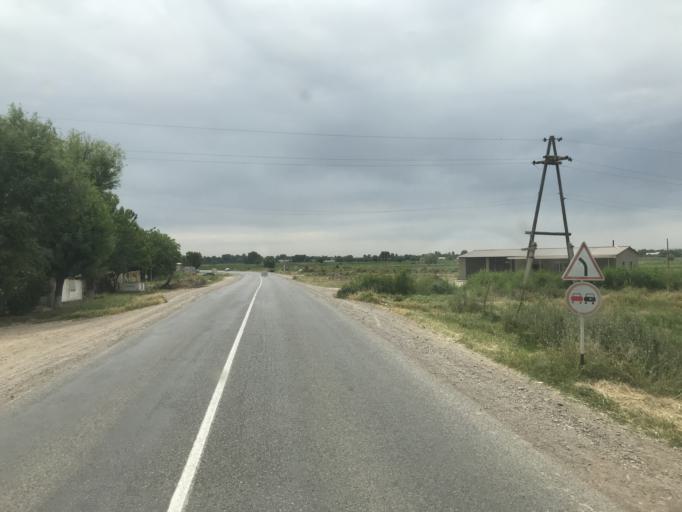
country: UZ
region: Toshkent
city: Yangiyul
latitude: 41.3352
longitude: 68.9270
